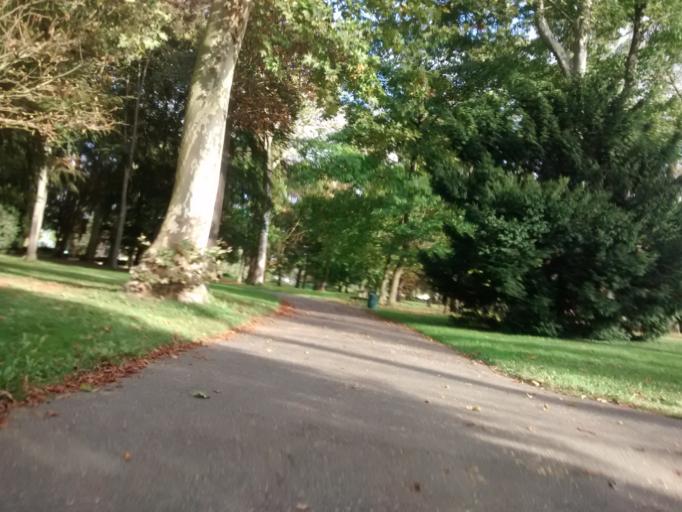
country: FR
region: Ile-de-France
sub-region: Departement du Val-de-Marne
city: L'Hay-les-Roses
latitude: 48.7745
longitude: 2.3326
